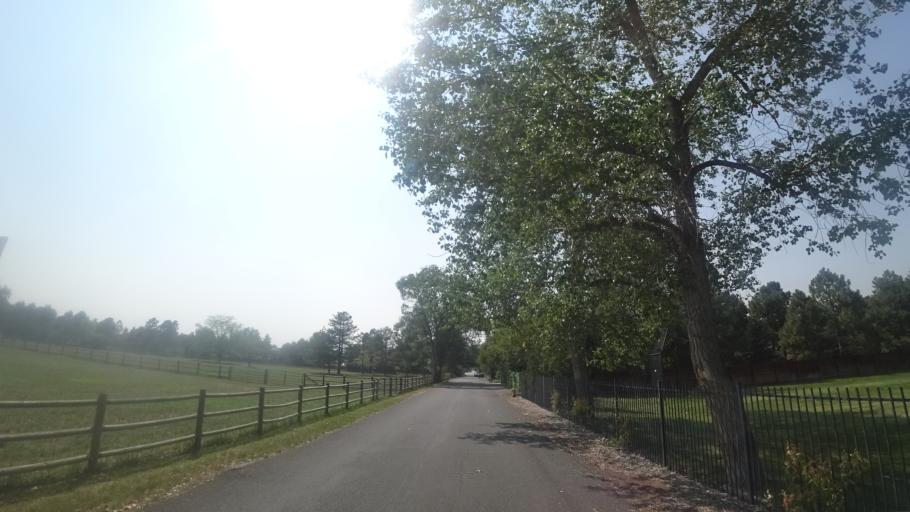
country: US
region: Colorado
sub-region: Arapahoe County
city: Englewood
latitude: 39.6368
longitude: -104.9756
